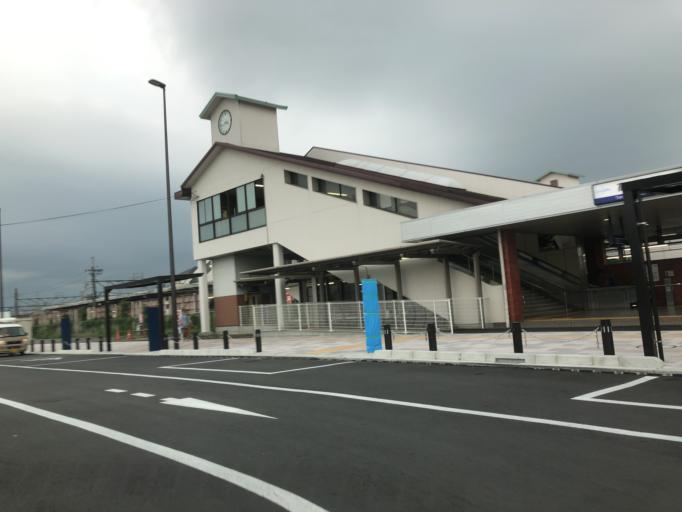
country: JP
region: Saitama
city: Sakado
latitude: 36.0032
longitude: 139.3980
